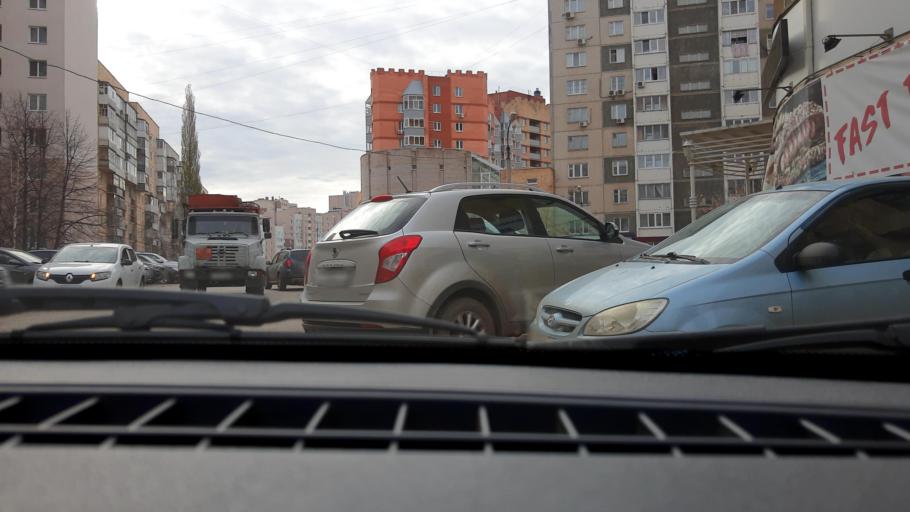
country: RU
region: Bashkortostan
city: Ufa
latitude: 54.7108
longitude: 55.9964
